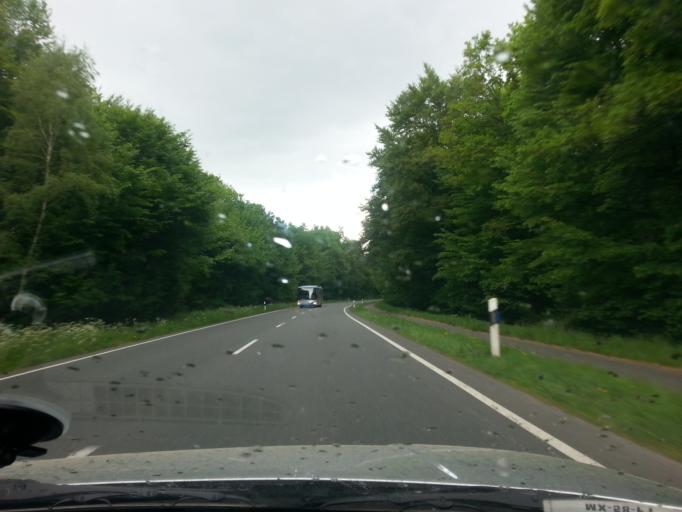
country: DE
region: Lower Saxony
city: Bad Bentheim
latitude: 52.3200
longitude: 7.1566
